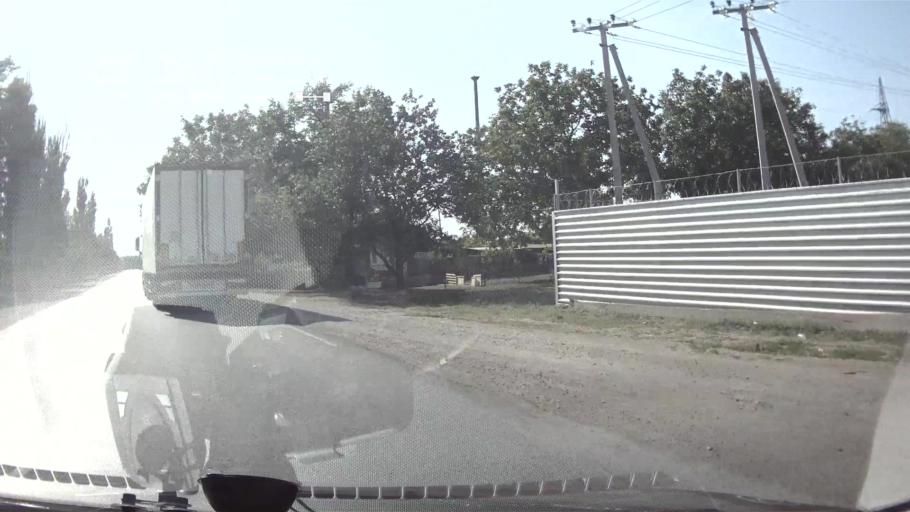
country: RU
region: Krasnodarskiy
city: Belaya Glina
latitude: 46.0893
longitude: 40.8302
